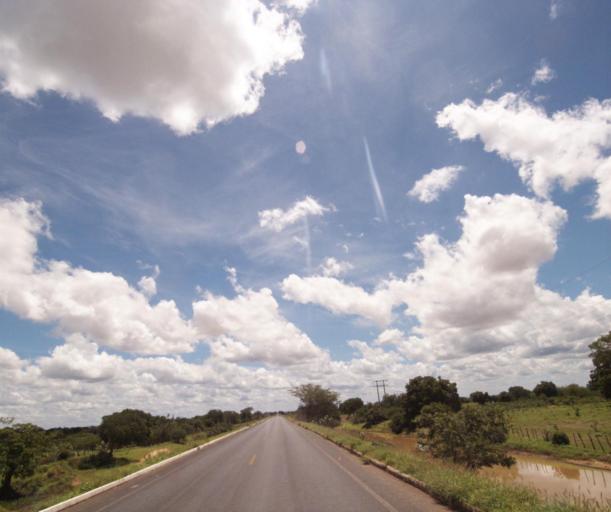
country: BR
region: Bahia
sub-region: Bom Jesus Da Lapa
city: Bom Jesus da Lapa
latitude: -13.2576
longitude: -43.4646
